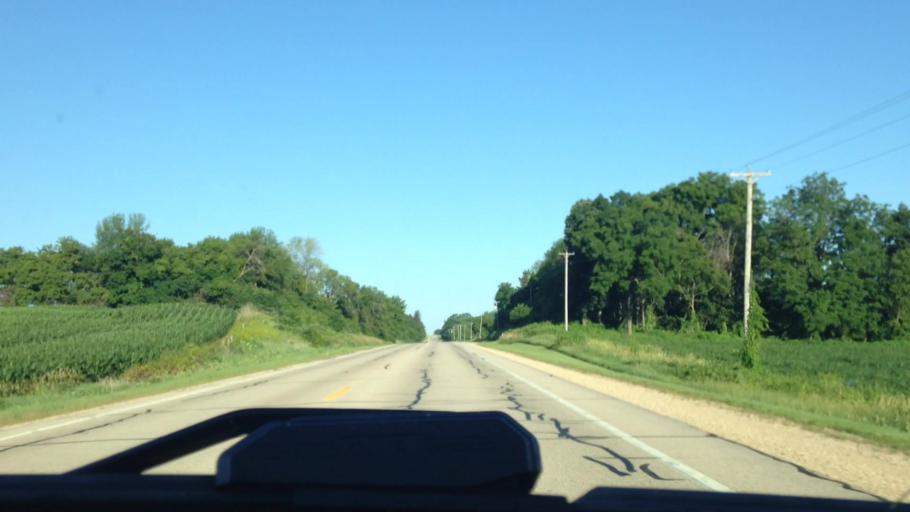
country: US
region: Wisconsin
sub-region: Dane County
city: De Forest
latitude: 43.3327
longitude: -89.2733
